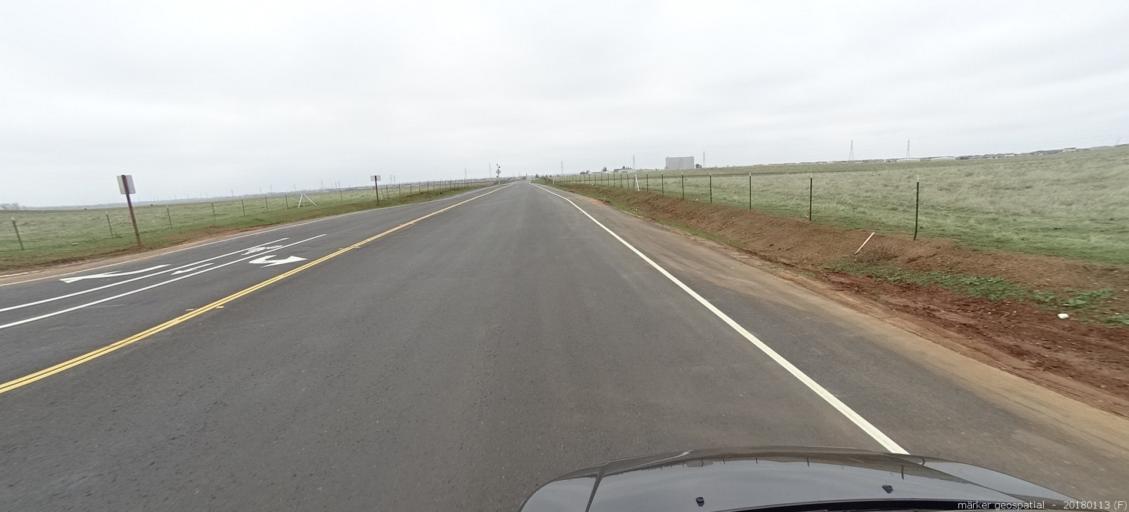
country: US
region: California
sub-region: Sacramento County
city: Gold River
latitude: 38.5592
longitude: -121.1877
